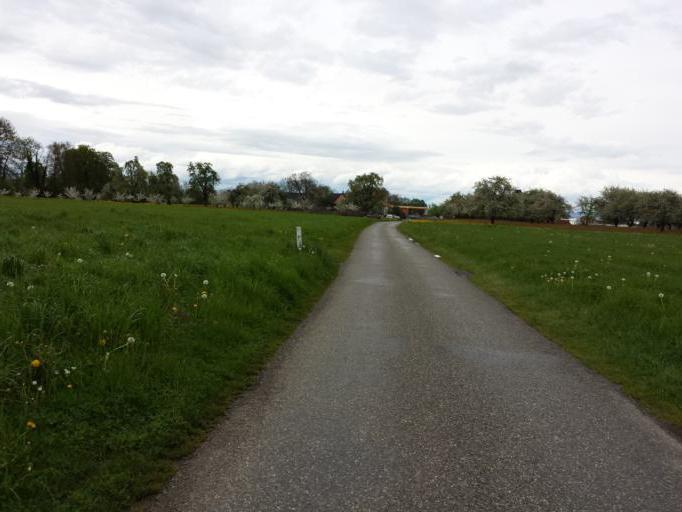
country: CH
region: Thurgau
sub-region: Arbon District
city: Egnach
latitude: 47.5458
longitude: 9.3697
